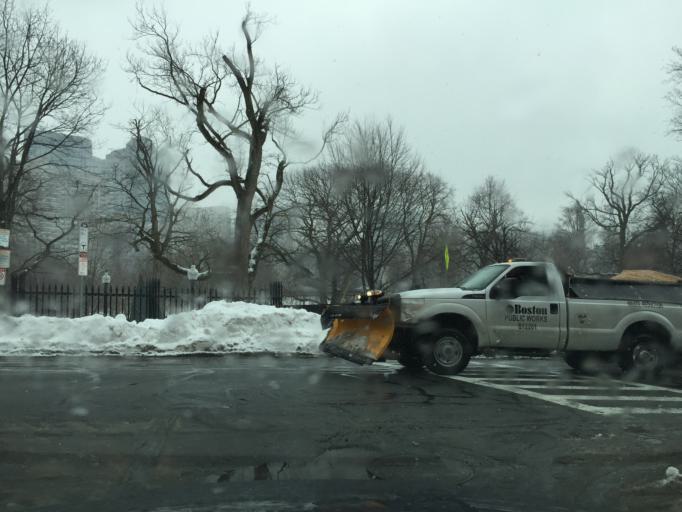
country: US
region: Massachusetts
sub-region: Suffolk County
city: Boston
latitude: 42.3572
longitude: -71.0658
